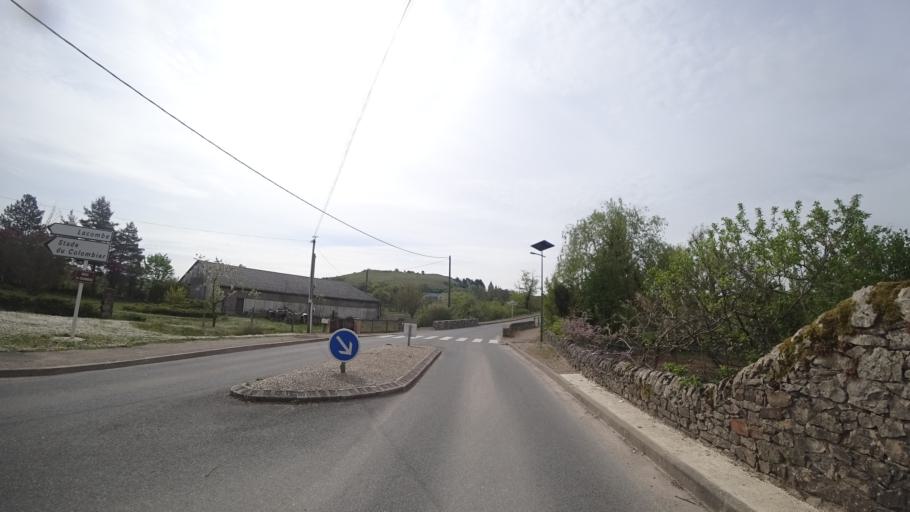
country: FR
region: Midi-Pyrenees
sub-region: Departement de l'Aveyron
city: Sebazac-Concoures
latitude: 44.3763
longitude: 2.6068
